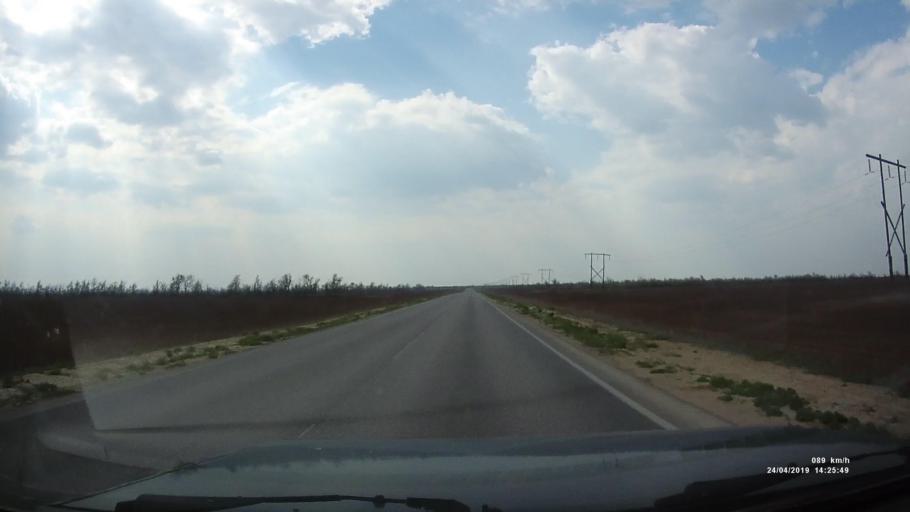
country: RU
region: Kalmykiya
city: Arshan'
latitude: 46.3316
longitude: 44.0751
